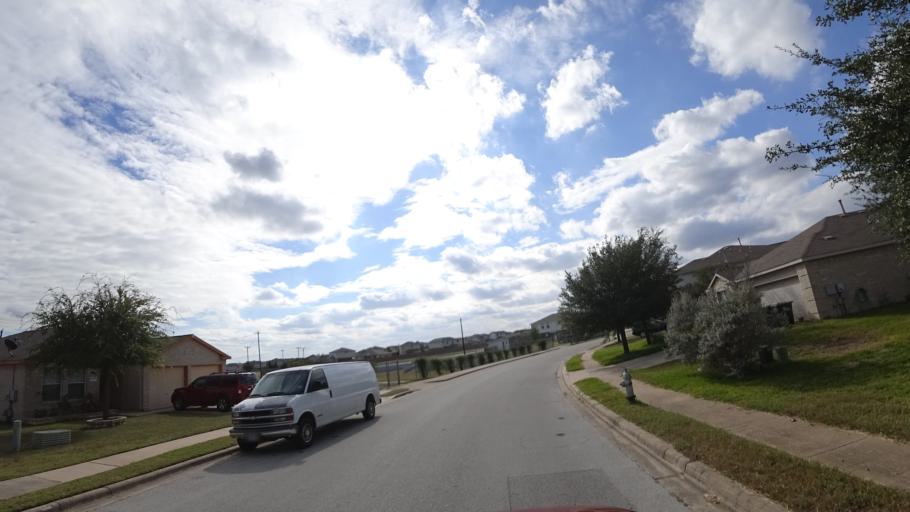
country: US
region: Texas
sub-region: Travis County
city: Pflugerville
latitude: 30.4304
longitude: -97.6367
